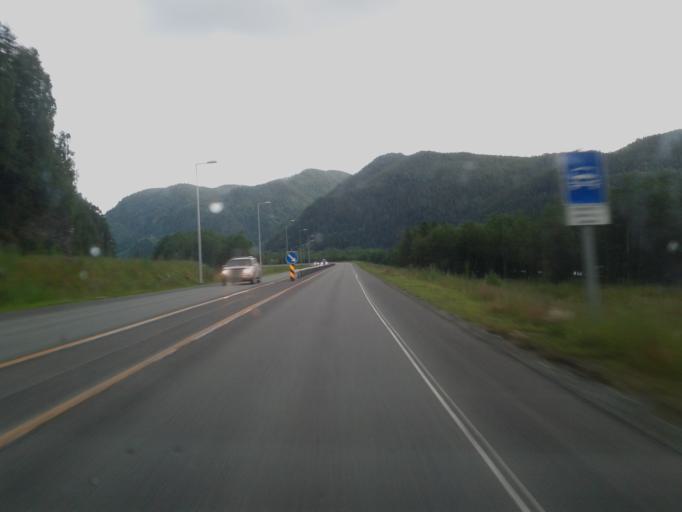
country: NO
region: Sor-Trondelag
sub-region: Midtre Gauldal
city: Storen
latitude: 63.0887
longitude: 10.2502
